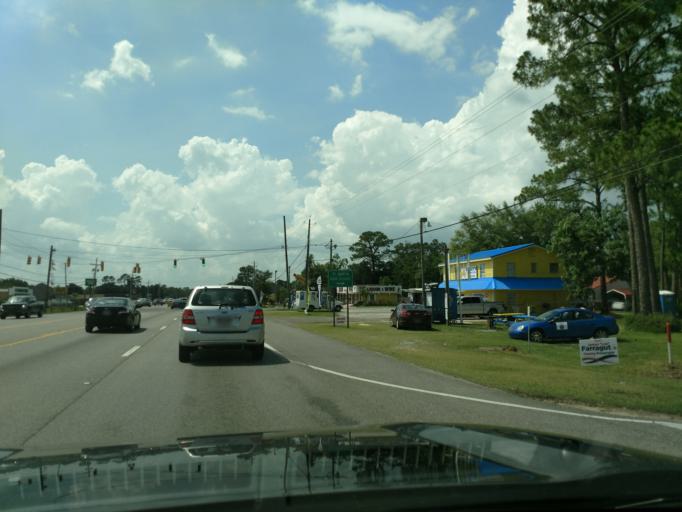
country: US
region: Mississippi
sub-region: Jackson County
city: Gulf Hills
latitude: 30.4380
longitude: -88.8329
